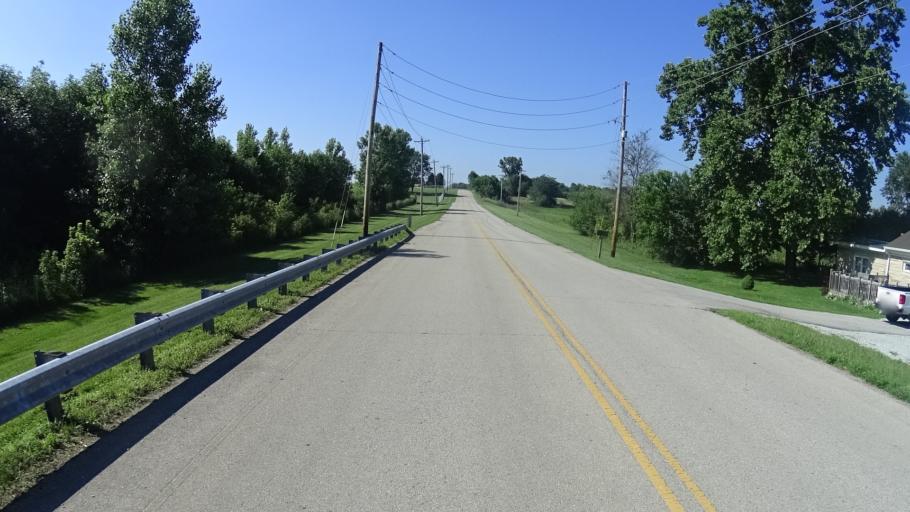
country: US
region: Indiana
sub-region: Madison County
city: Ingalls
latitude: 39.9701
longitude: -85.7962
